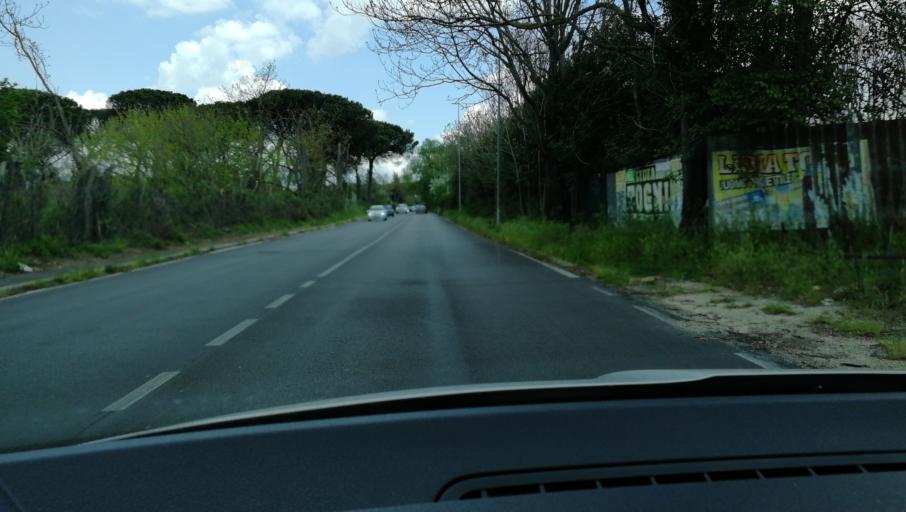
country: IT
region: Latium
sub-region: Citta metropolitana di Roma Capitale
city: Rome
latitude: 41.8566
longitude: 12.5316
